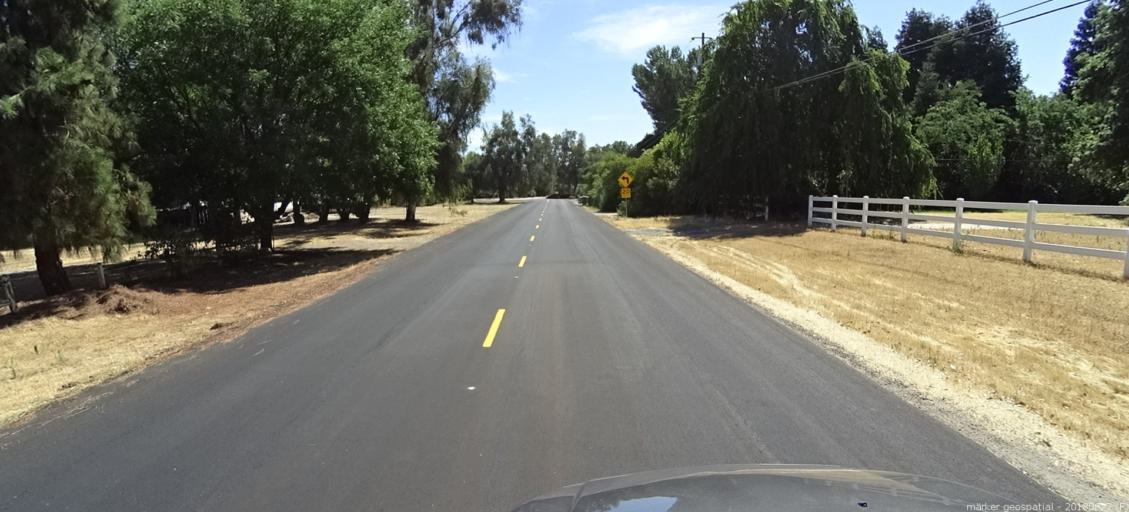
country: US
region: California
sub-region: Madera County
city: Bonadelle Ranchos-Madera Ranchos
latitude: 36.9200
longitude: -119.8738
